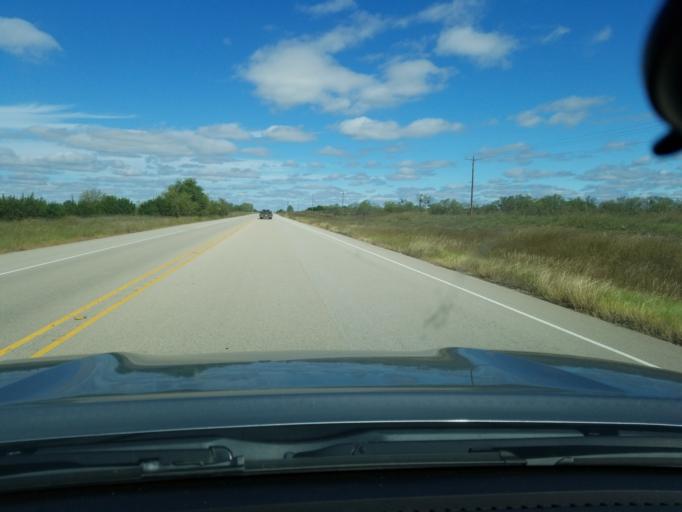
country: US
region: Texas
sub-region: Hamilton County
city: Hamilton
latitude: 31.6597
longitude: -98.1425
